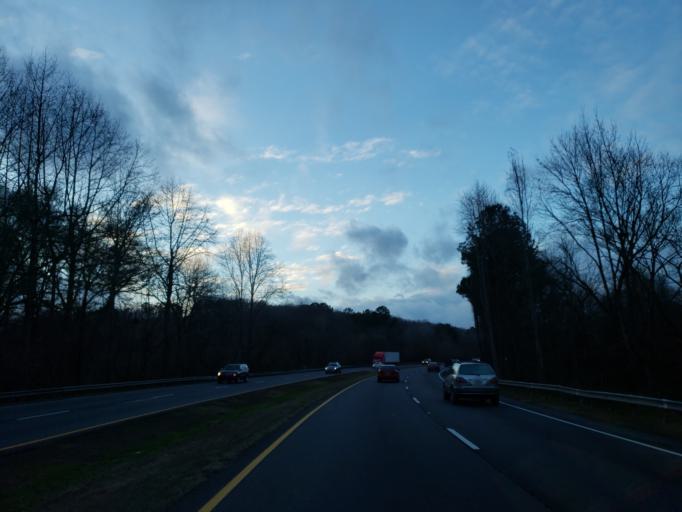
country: US
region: Georgia
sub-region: Fulton County
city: Union City
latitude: 33.6593
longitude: -84.5342
